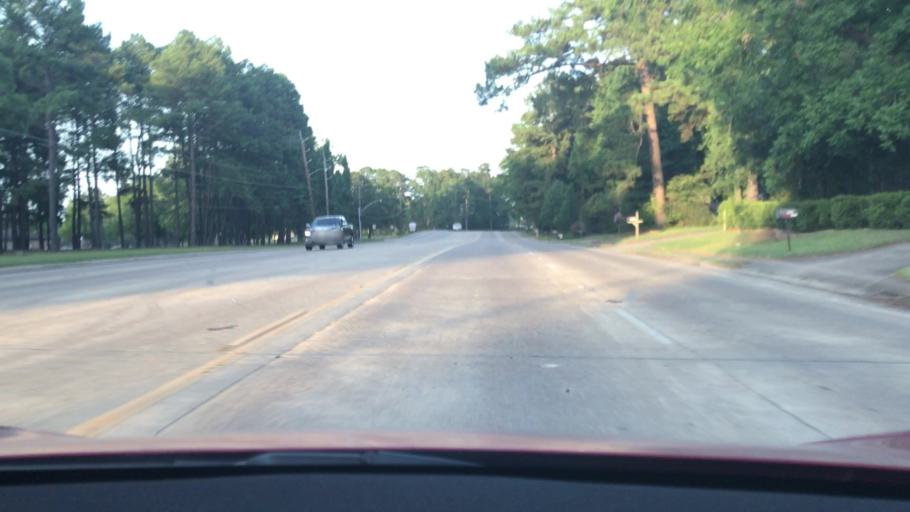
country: US
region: Louisiana
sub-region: De Soto Parish
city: Stonewall
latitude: 32.4020
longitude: -93.7877
